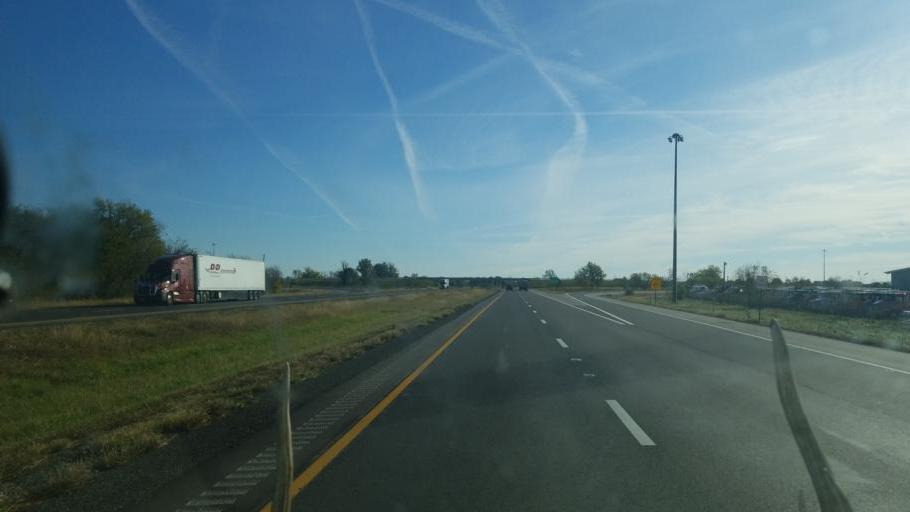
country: US
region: Illinois
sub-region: Madison County
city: Highland
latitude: 38.7862
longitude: -89.6365
